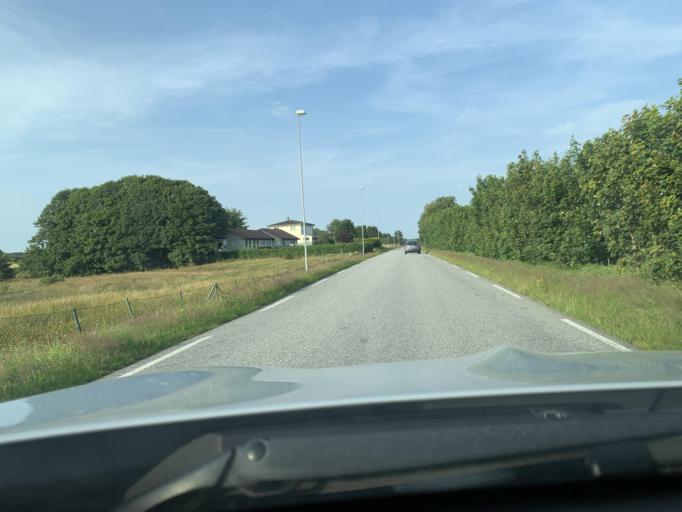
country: NO
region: Rogaland
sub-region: Time
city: Bryne
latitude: 58.7368
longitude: 5.6066
